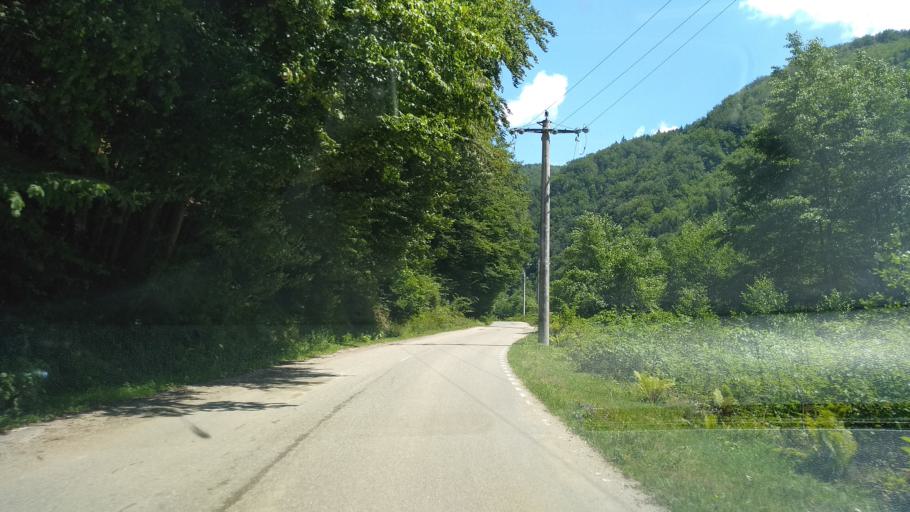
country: RO
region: Hunedoara
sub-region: Comuna Orastioara de Sus
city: Orastioara de Sus
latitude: 45.6218
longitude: 23.2298
